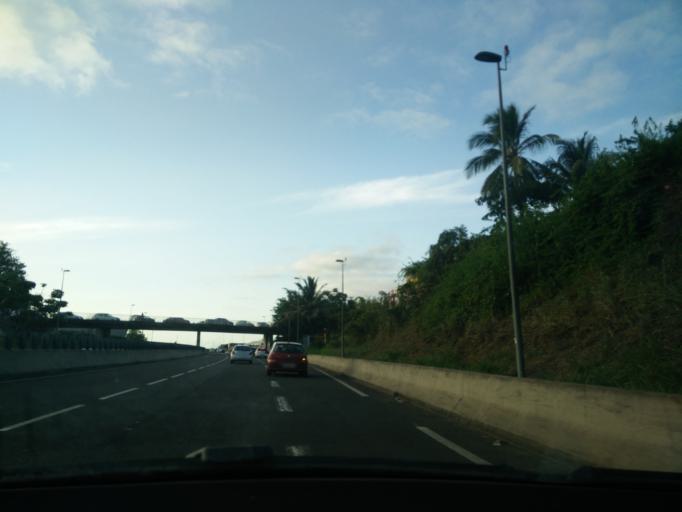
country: GP
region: Guadeloupe
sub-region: Guadeloupe
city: Les Abymes
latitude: 16.2638
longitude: -61.5111
